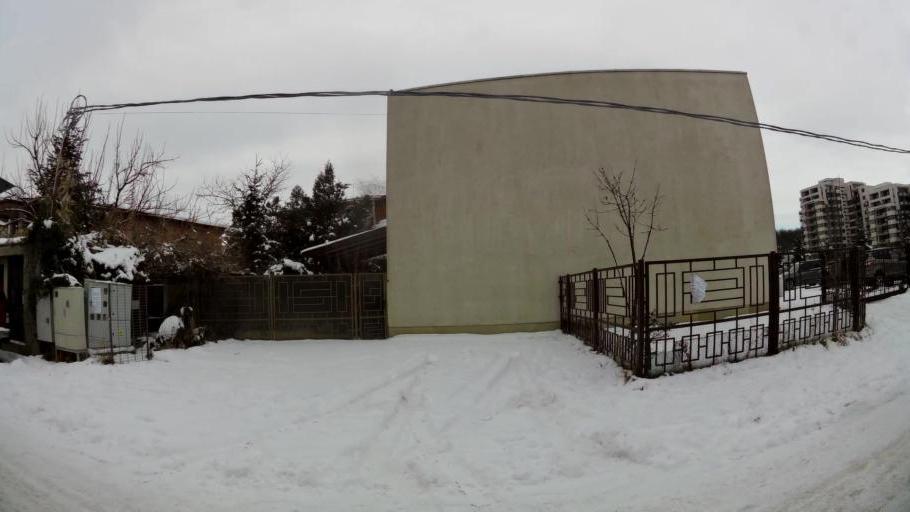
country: RO
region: Ilfov
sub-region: Comuna Tunari
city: Tunari
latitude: 44.5206
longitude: 26.1460
